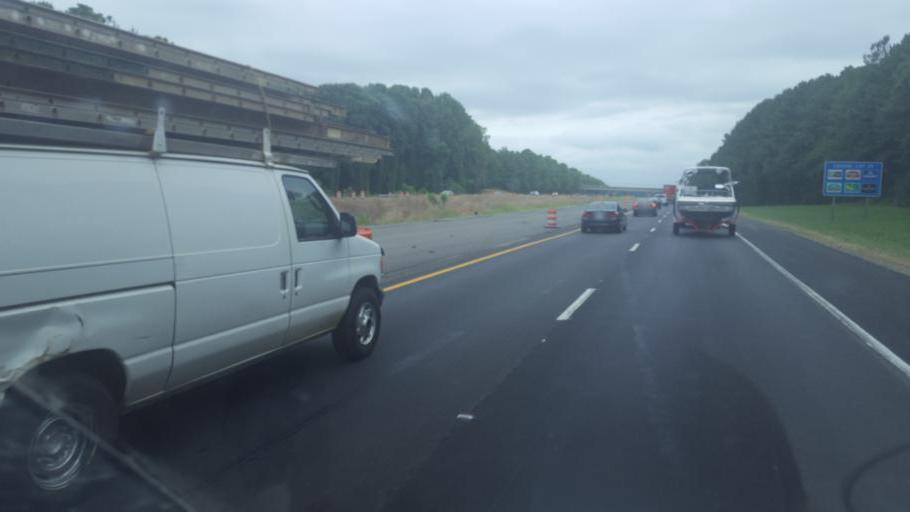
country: US
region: North Carolina
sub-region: Mecklenburg County
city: Huntersville
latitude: 35.4178
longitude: -80.8599
